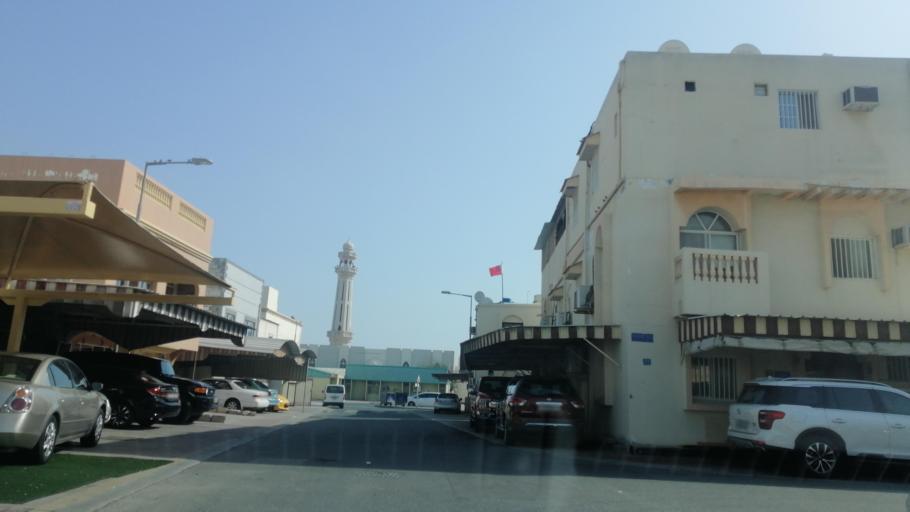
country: BH
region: Muharraq
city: Al Muharraq
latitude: 26.2570
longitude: 50.6311
